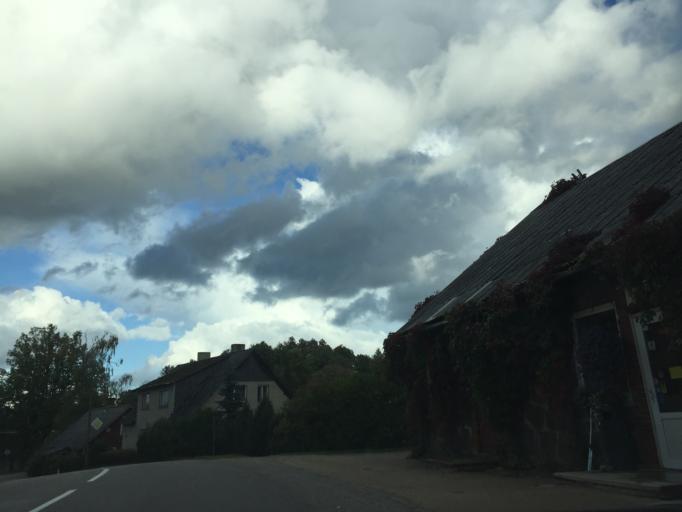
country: LV
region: Amatas Novads
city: Drabesi
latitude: 57.0695
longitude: 25.1918
